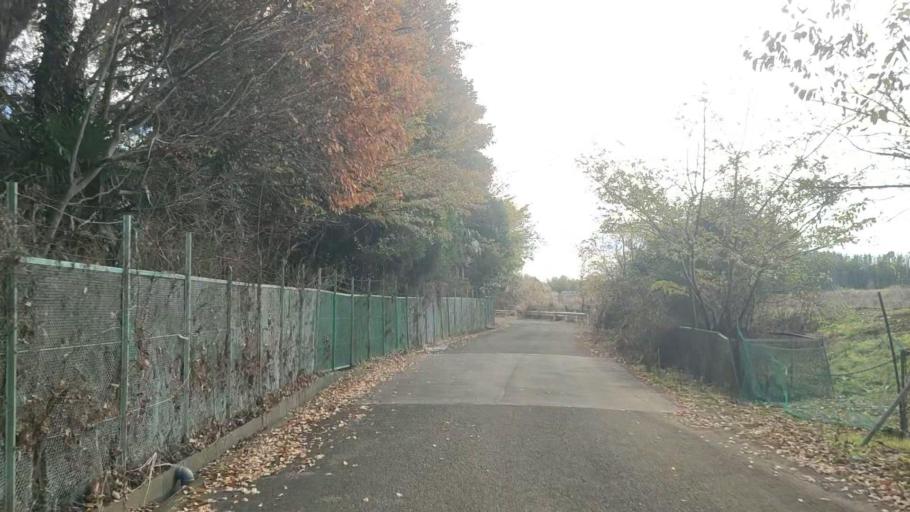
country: JP
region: Kanagawa
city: Minami-rinkan
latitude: 35.4904
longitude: 139.4923
